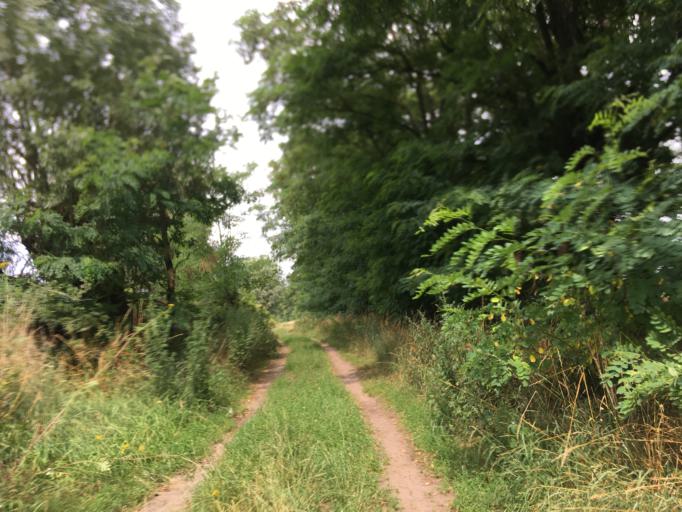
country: DE
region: Brandenburg
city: Bernau bei Berlin
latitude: 52.6312
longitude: 13.5848
